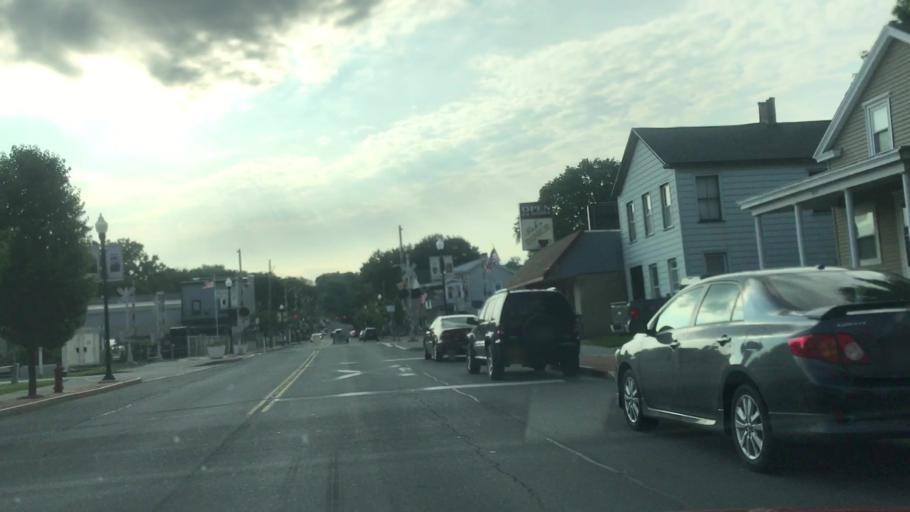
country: US
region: New York
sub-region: Albany County
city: Watervliet
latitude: 42.7324
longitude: -73.7096
